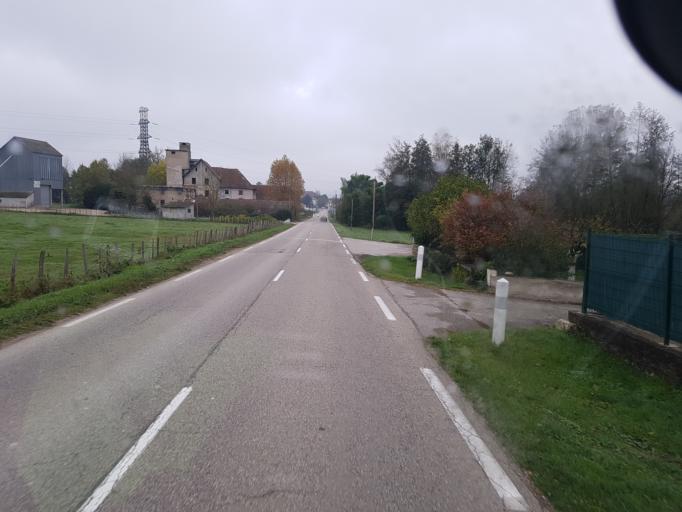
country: FR
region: Rhone-Alpes
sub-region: Departement de l'Isere
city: Chimilin
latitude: 45.5797
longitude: 5.6053
